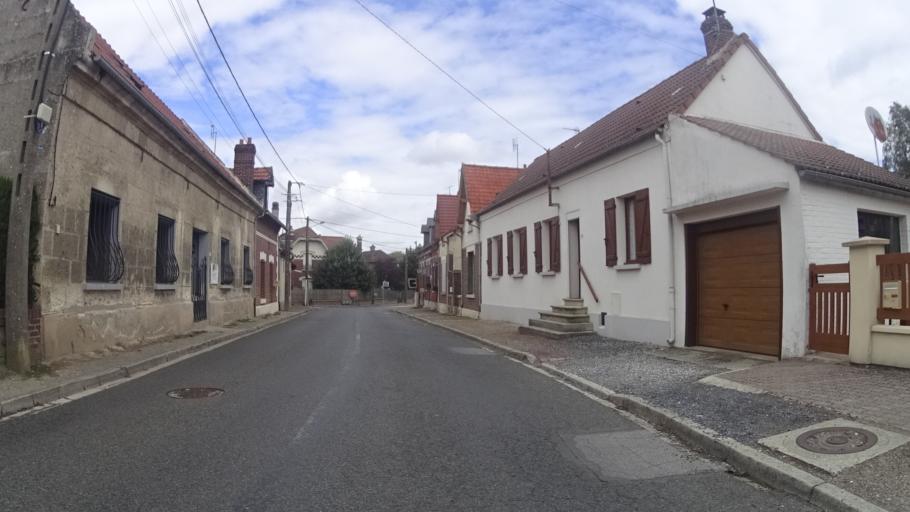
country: FR
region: Picardie
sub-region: Departement de l'Oise
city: Noyon
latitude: 49.5579
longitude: 2.9929
